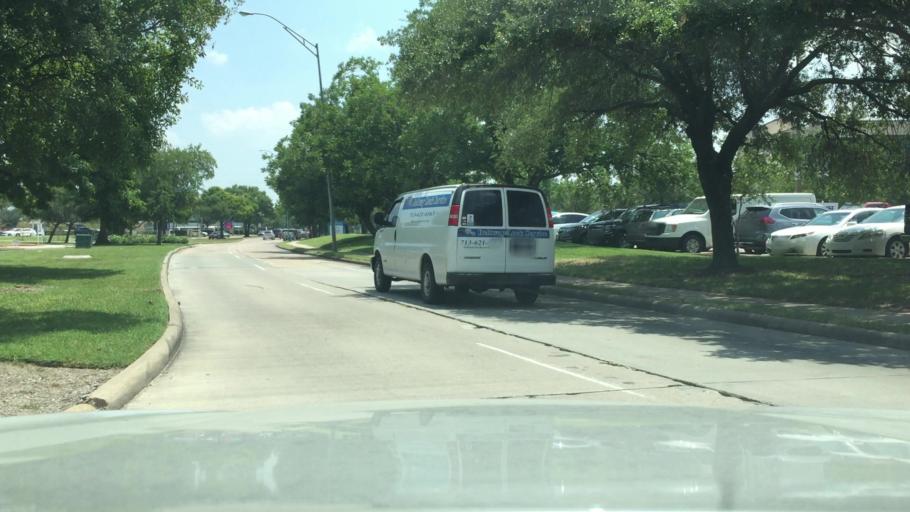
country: US
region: Texas
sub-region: Harris County
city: Bunker Hill Village
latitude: 29.7304
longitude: -95.5948
